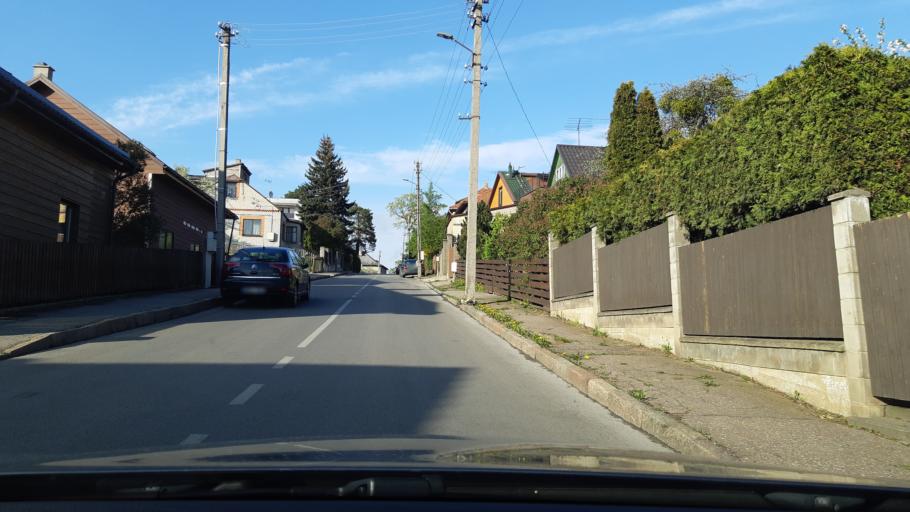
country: LT
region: Kauno apskritis
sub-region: Kaunas
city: Aleksotas
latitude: 54.8757
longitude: 23.9451
